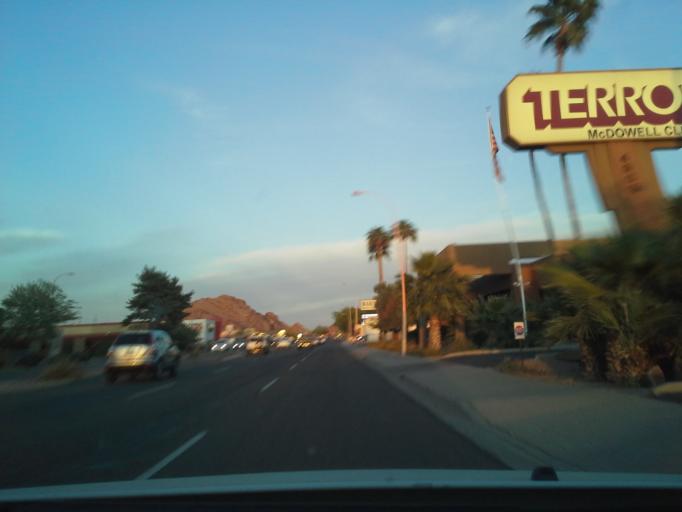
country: US
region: Arizona
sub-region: Maricopa County
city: Tempe Junction
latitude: 33.4655
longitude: -111.9766
